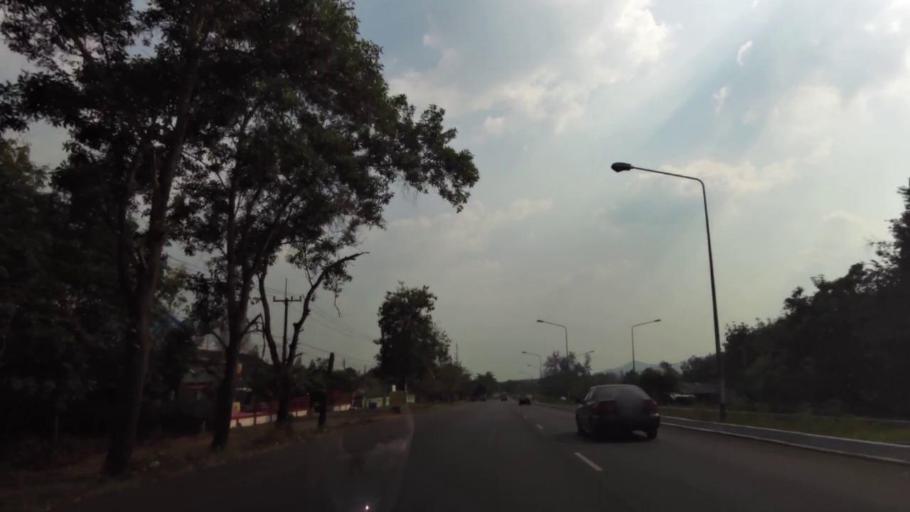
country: TH
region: Rayong
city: Wang Chan
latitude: 13.0357
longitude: 101.4350
